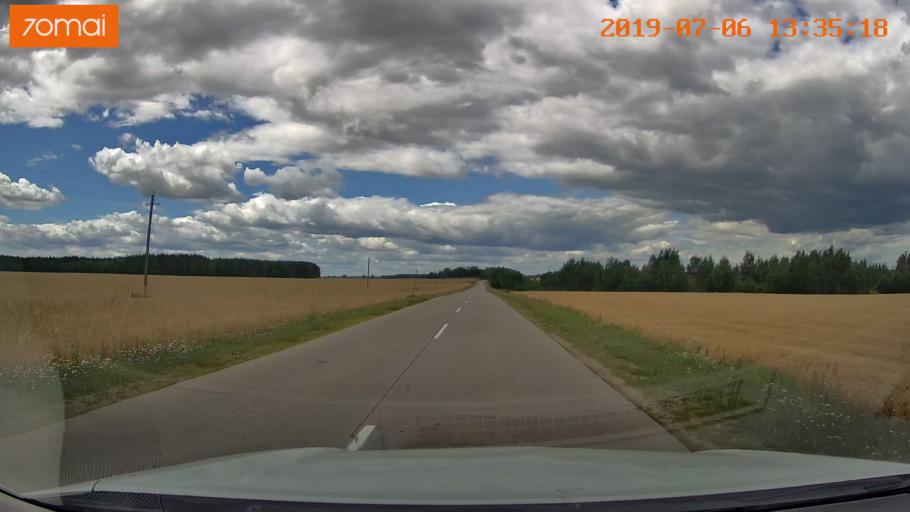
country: BY
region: Minsk
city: Enyerhyetykaw
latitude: 53.6811
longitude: 26.8828
